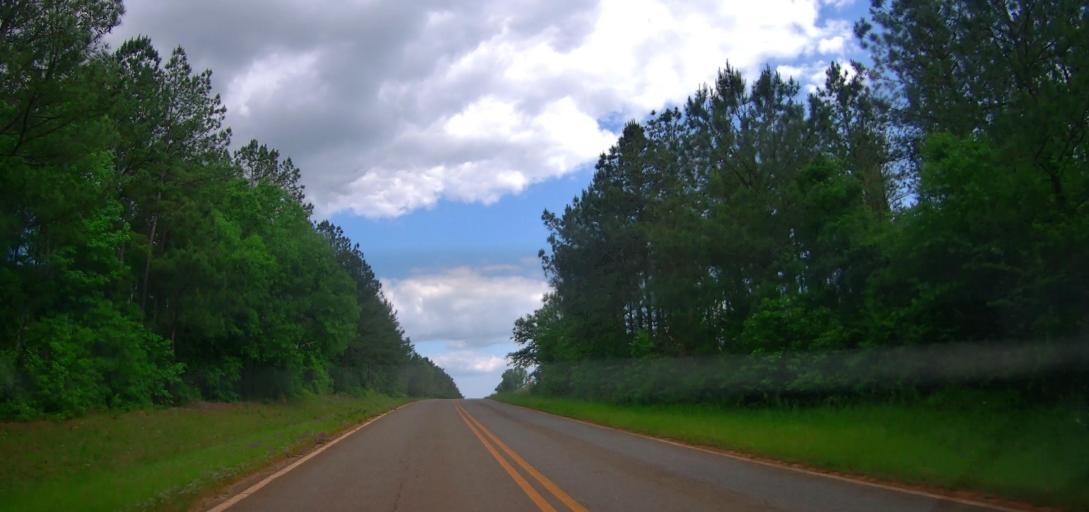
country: US
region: Georgia
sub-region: Laurens County
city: East Dublin
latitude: 32.7377
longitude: -82.9158
